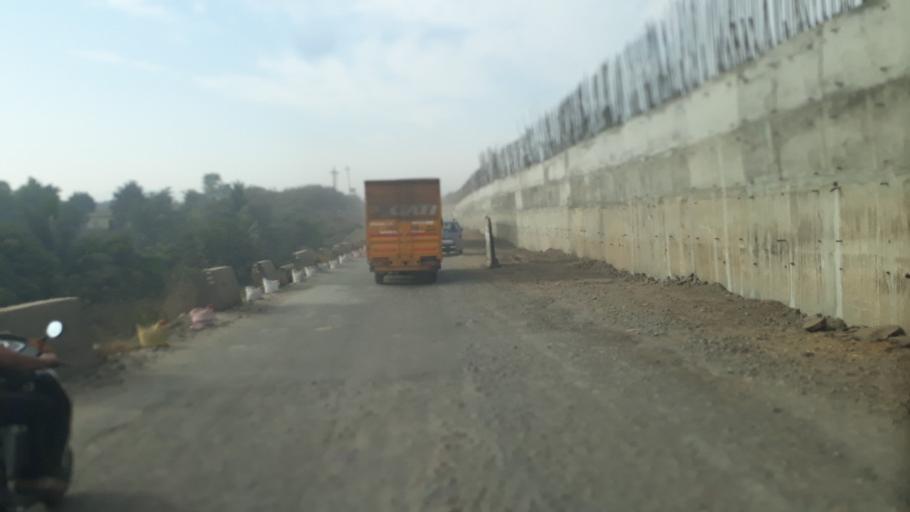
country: IN
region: Maharashtra
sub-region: Raigarh
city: Pen
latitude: 18.7721
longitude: 73.0928
